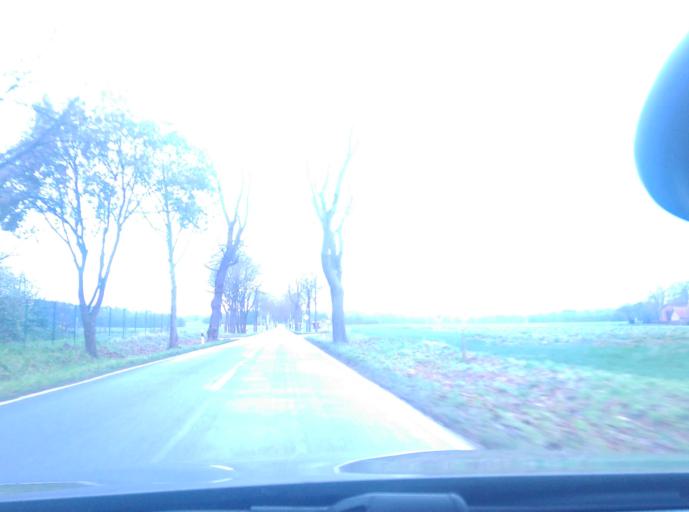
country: DE
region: Lower Saxony
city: Lindwedel
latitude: 52.5801
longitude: 9.6655
